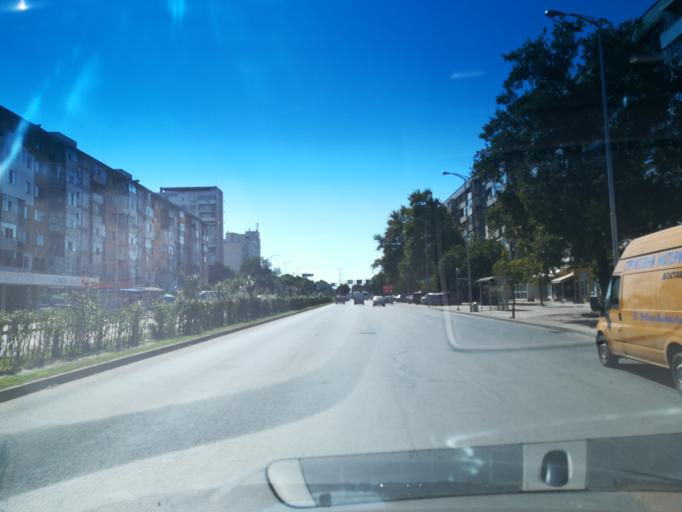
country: BG
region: Plovdiv
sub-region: Obshtina Plovdiv
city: Plovdiv
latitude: 42.1590
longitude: 24.7348
